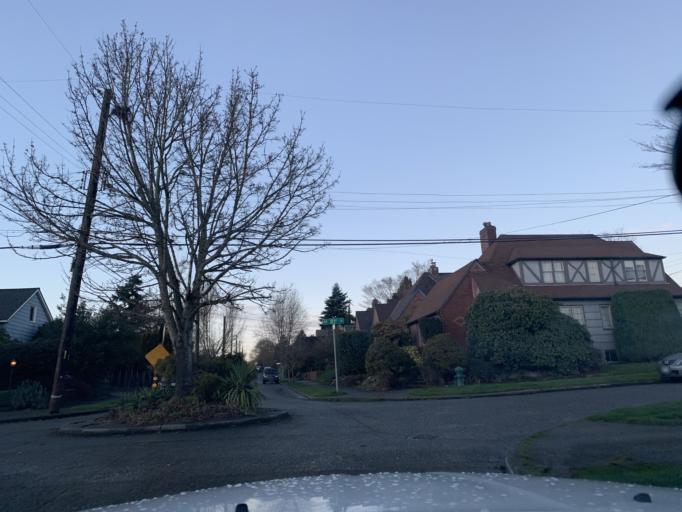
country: US
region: Washington
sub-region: King County
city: Shoreline
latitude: 47.6874
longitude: -122.3243
